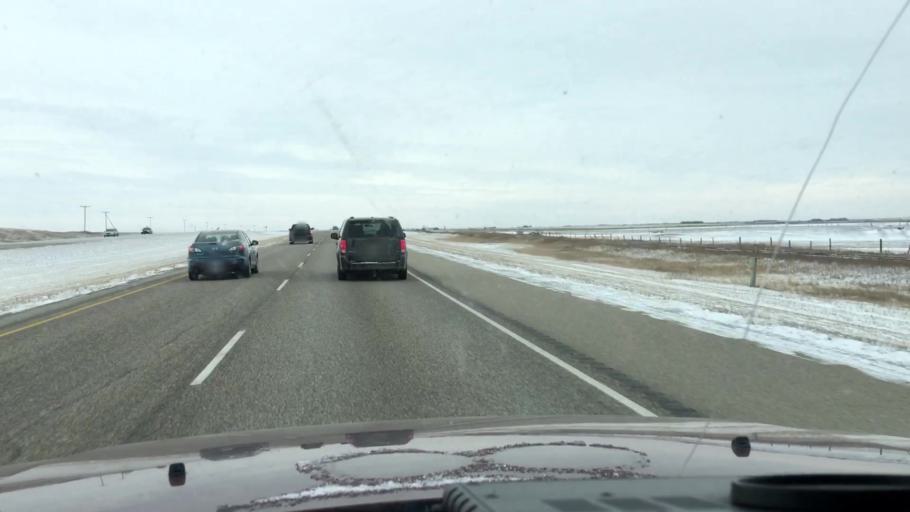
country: CA
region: Saskatchewan
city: Saskatoon
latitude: 51.5940
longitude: -106.3857
